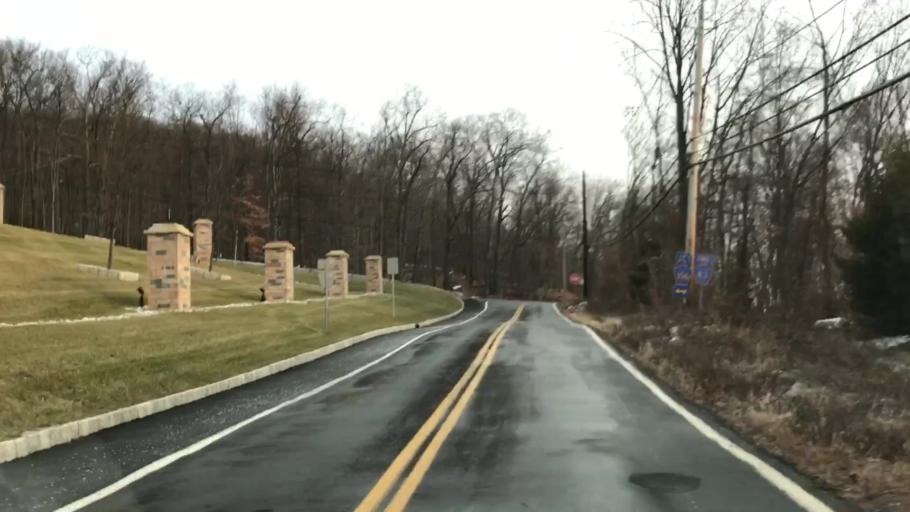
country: US
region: New York
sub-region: Rockland County
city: Thiells
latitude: 41.2308
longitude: -74.0444
